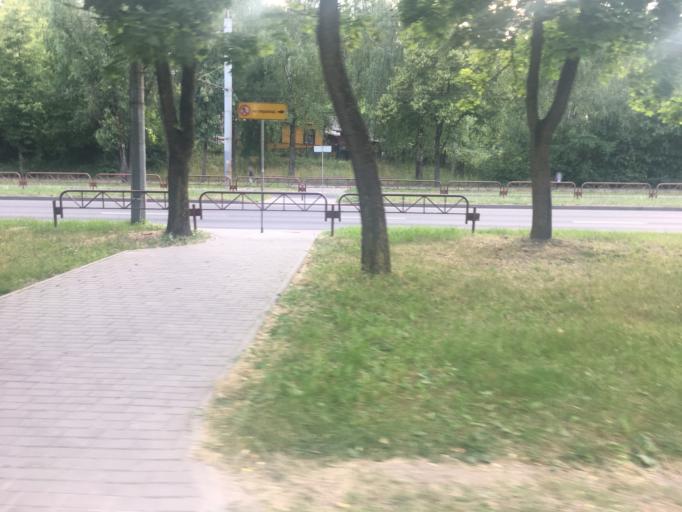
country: BY
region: Grodnenskaya
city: Hrodna
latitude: 53.6820
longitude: 23.8077
